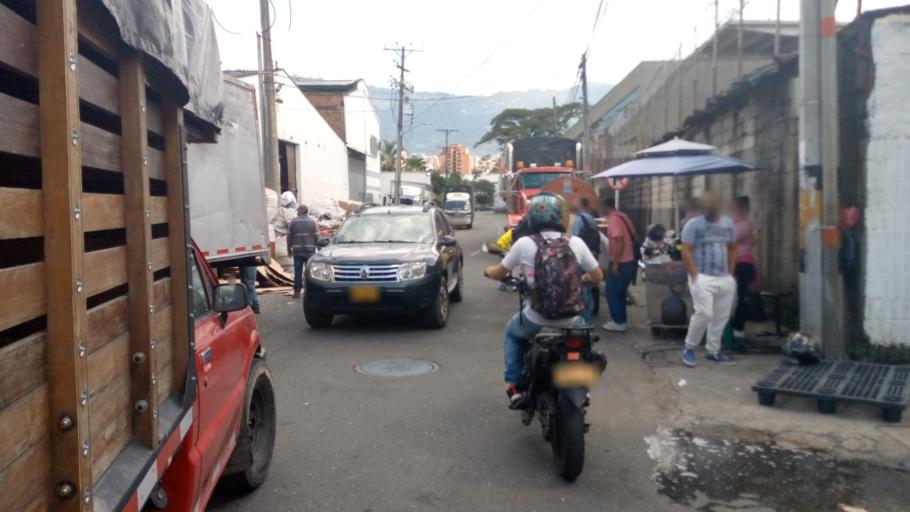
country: CO
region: Antioquia
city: Envigado
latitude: 6.1810
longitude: -75.5932
